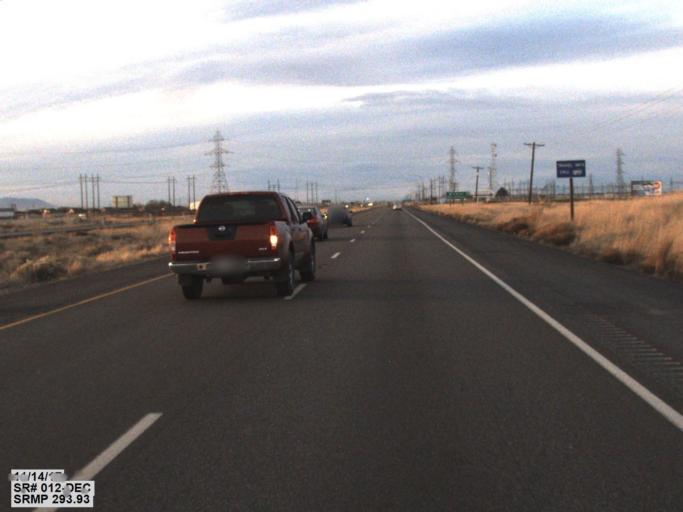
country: US
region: Washington
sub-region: Walla Walla County
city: Burbank
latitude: 46.2239
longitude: -119.0340
